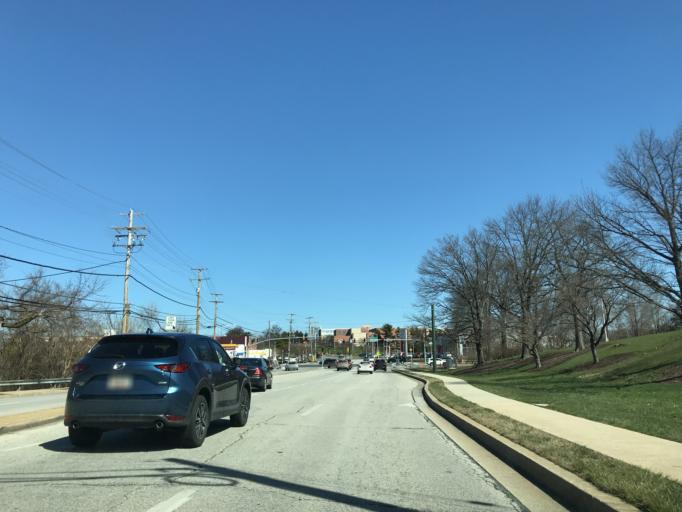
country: US
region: Maryland
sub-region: Baltimore County
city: Woodlawn
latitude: 39.3110
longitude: -76.7349
